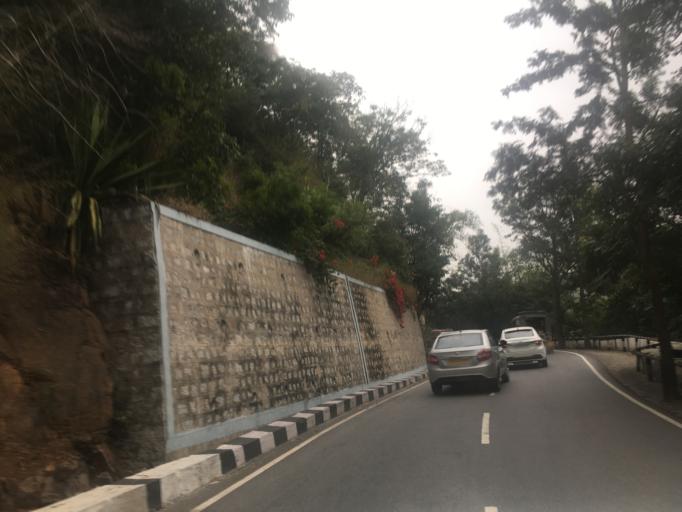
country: IN
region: Andhra Pradesh
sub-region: Chittoor
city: Tirumala
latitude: 13.6669
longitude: 79.3509
